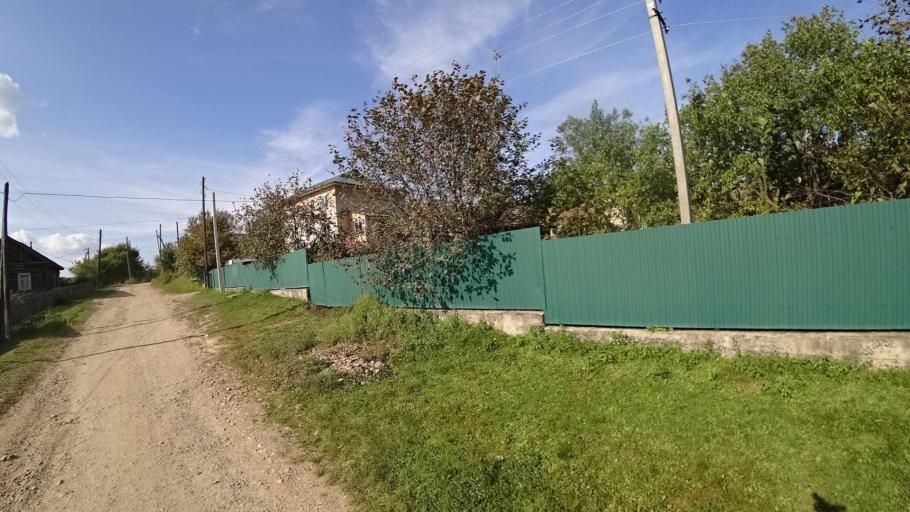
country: RU
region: Jewish Autonomous Oblast
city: Birakan
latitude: 48.9968
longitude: 131.7233
